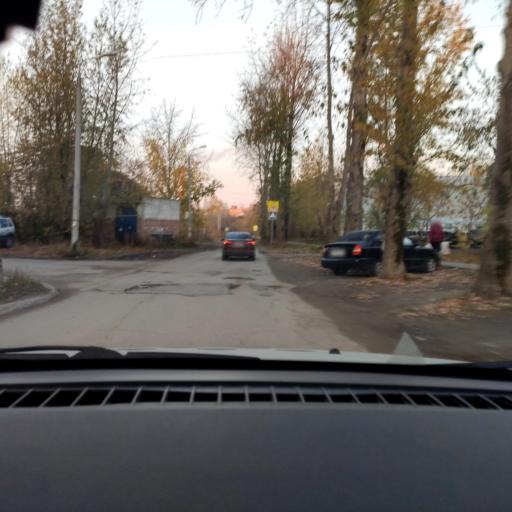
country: RU
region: Perm
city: Perm
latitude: 58.0598
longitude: 56.3589
